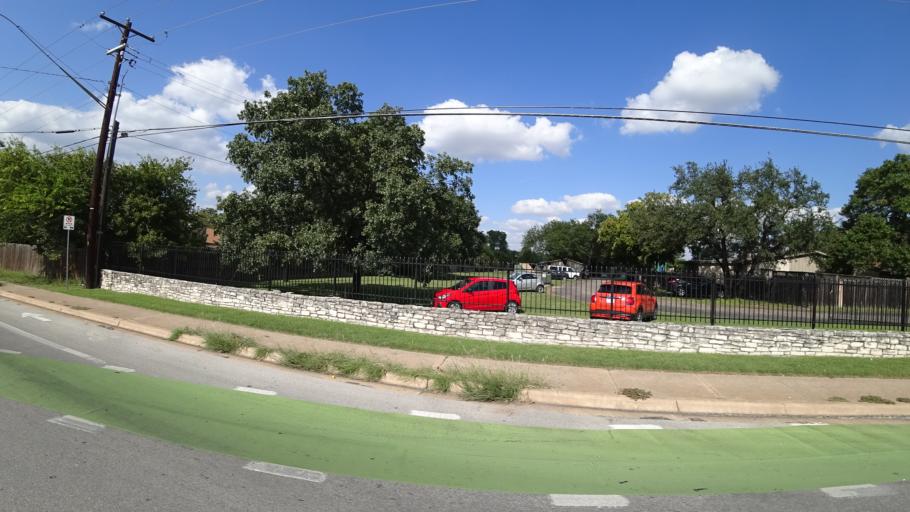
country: US
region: Texas
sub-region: Travis County
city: Wells Branch
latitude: 30.3642
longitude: -97.7143
